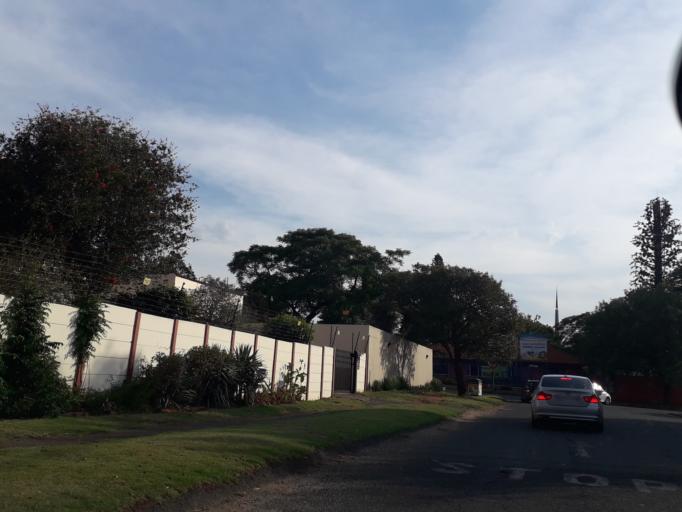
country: ZA
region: Gauteng
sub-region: City of Johannesburg Metropolitan Municipality
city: Johannesburg
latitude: -26.1224
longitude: 27.9986
